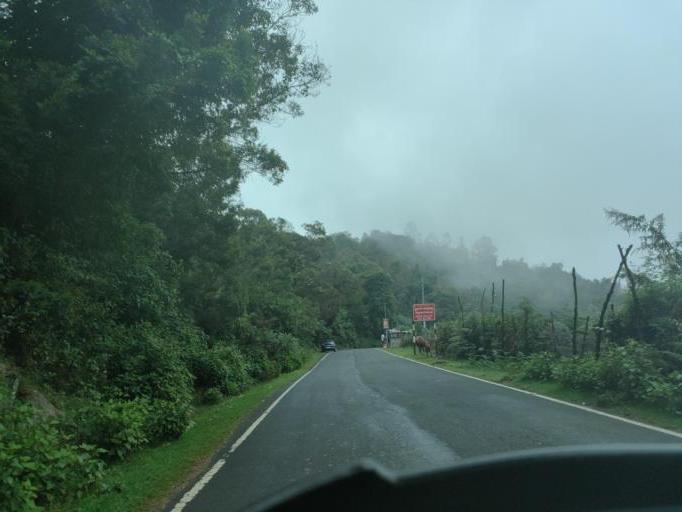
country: IN
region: Tamil Nadu
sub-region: Dindigul
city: Kodaikanal
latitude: 10.2501
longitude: 77.4131
